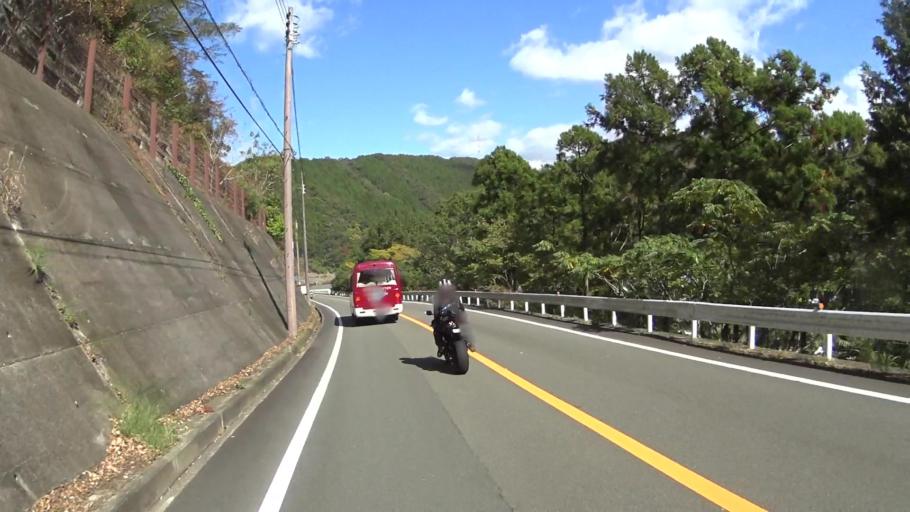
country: JP
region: Kyoto
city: Kameoka
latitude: 35.1492
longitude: 135.5153
